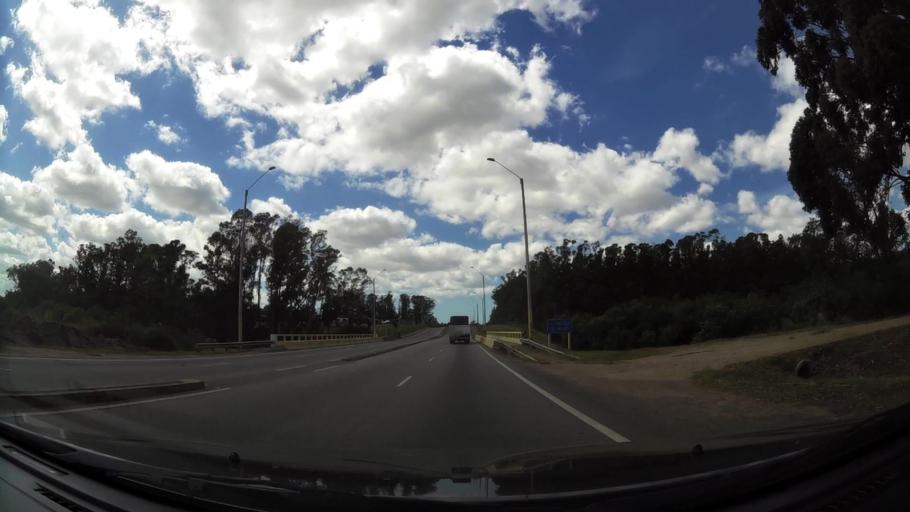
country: UY
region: Canelones
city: Colonia Nicolich
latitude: -34.8069
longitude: -56.0471
